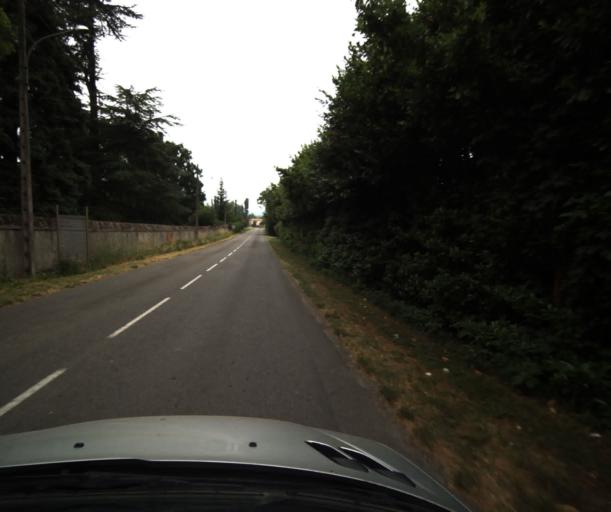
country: FR
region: Midi-Pyrenees
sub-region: Departement du Tarn-et-Garonne
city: Saint-Nicolas-de-la-Grave
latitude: 44.0655
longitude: 1.0234
